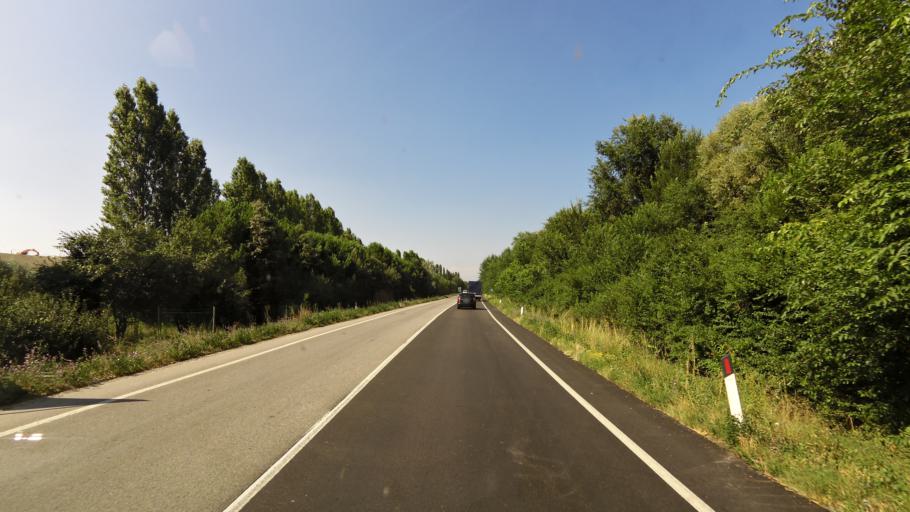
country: IT
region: Emilia-Romagna
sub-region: Provincia di Ravenna
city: Ravenna
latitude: 44.4734
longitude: 12.2095
